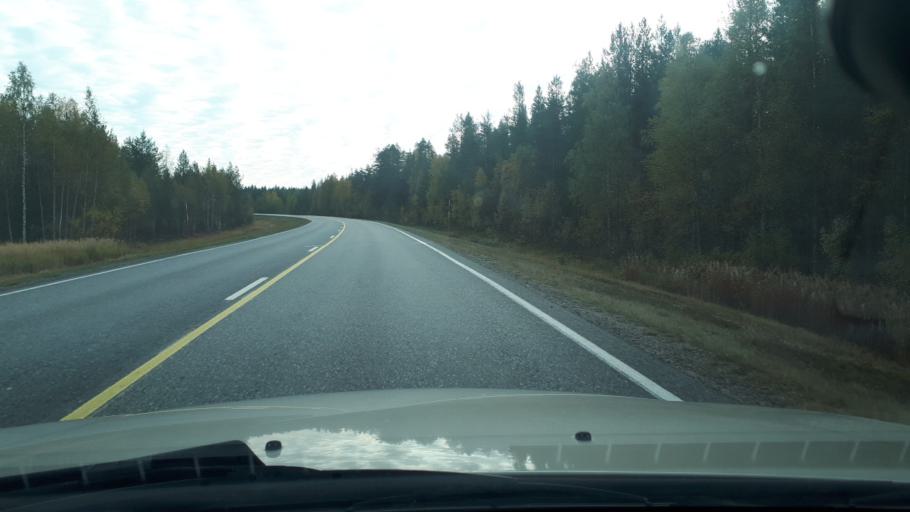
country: FI
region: Lapland
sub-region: Rovaniemi
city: Ranua
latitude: 65.9539
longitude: 26.4162
